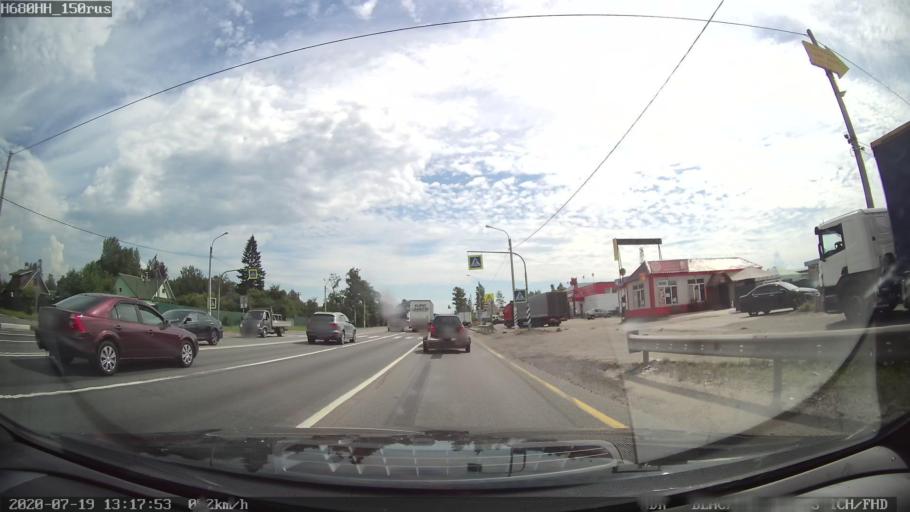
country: RU
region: St.-Petersburg
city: Kolpino
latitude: 59.7054
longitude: 30.5763
